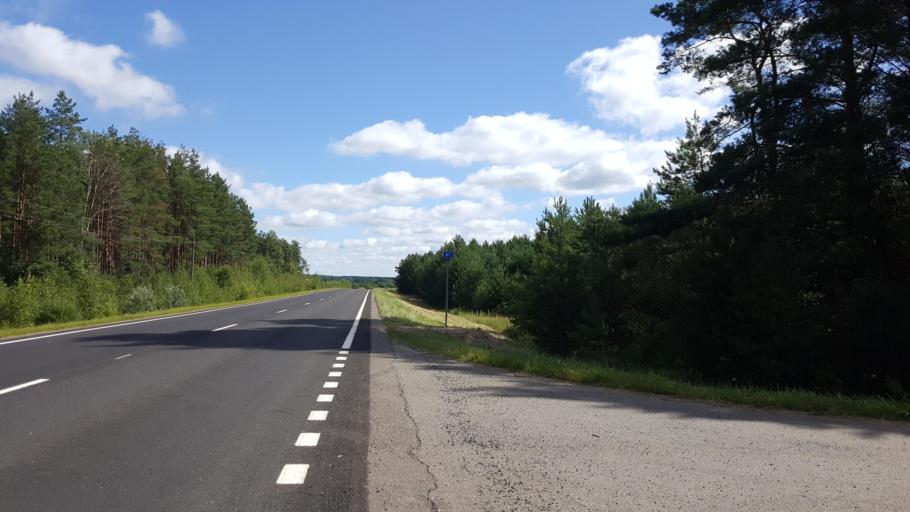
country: BY
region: Brest
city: Kamyanyets
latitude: 52.3976
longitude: 23.9901
